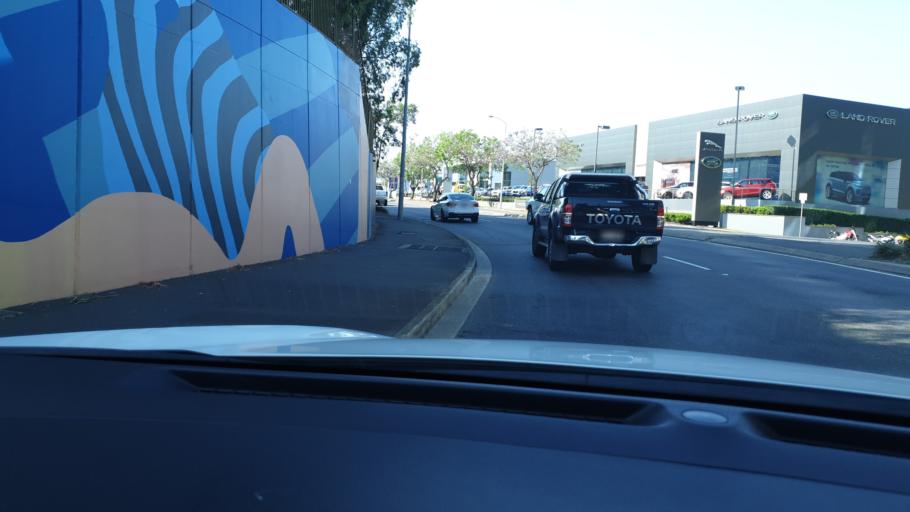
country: AU
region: Queensland
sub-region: Brisbane
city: Fortitude Valley
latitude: -27.4490
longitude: 153.0425
